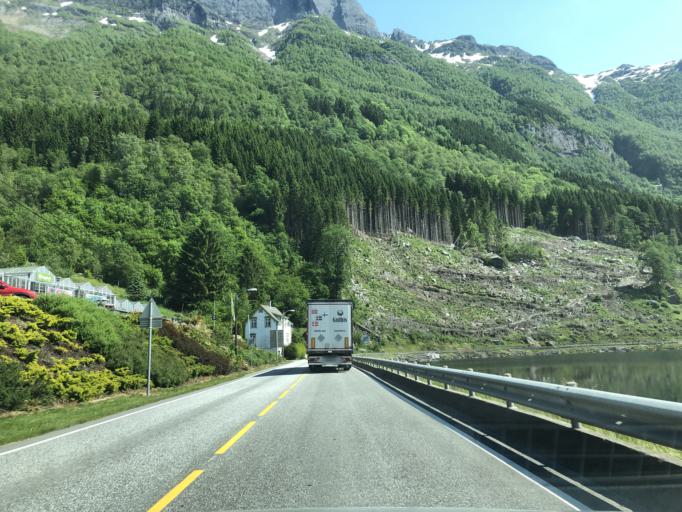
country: NO
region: Hordaland
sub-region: Odda
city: Odda
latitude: 60.0534
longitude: 6.5568
